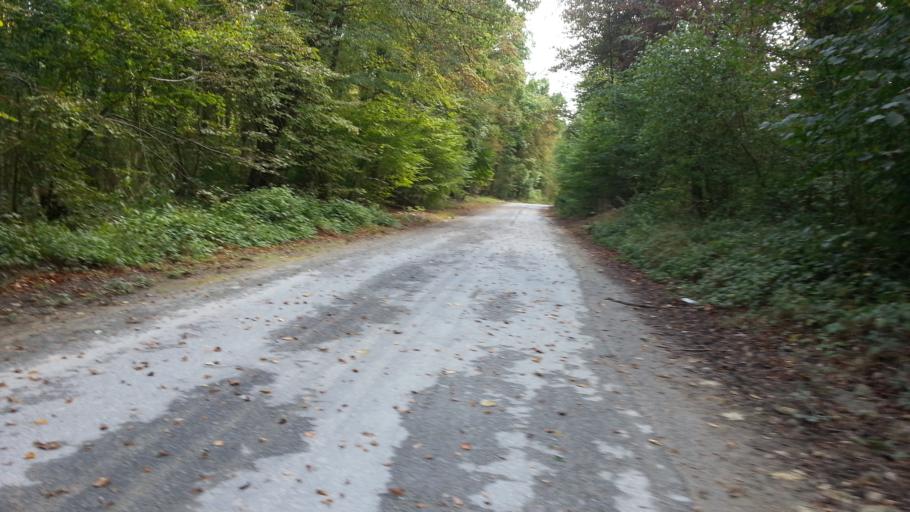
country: FR
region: Picardie
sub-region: Departement de l'Oise
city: Saint-Maximin
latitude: 49.2140
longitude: 2.4603
